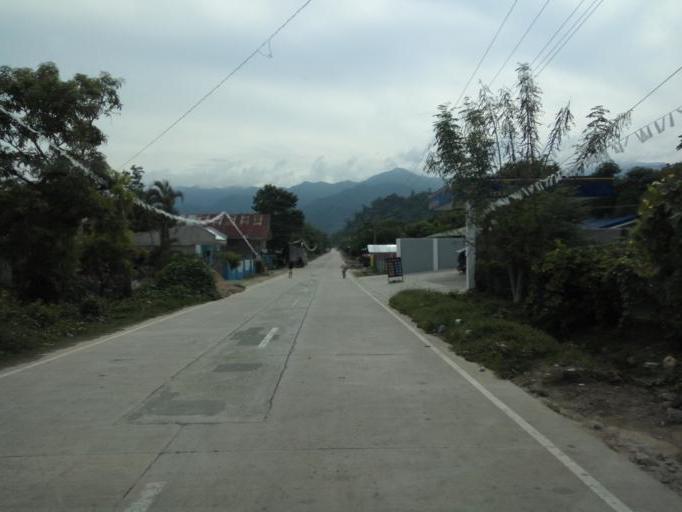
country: PH
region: Central Luzon
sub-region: Province of Aurora
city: Dinalongan
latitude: 16.0774
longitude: 121.7670
